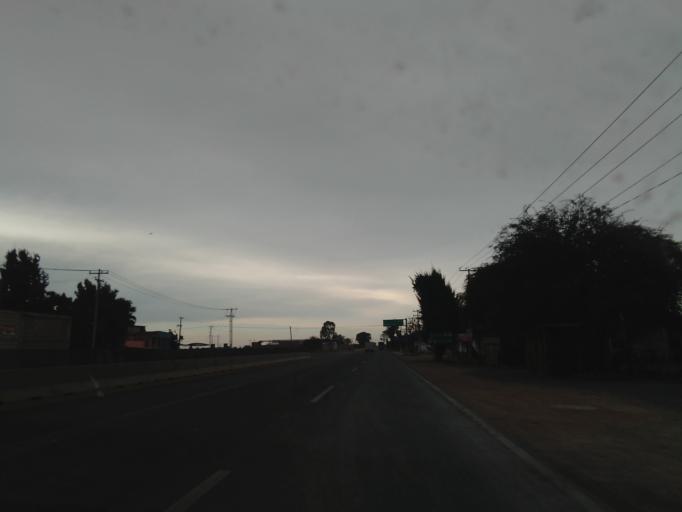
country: MX
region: Guanajuato
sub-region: Dolores Hidalgo Cuna de la Independencia Nacional
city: Ejido Jesus Maria
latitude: 21.1921
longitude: -100.8678
